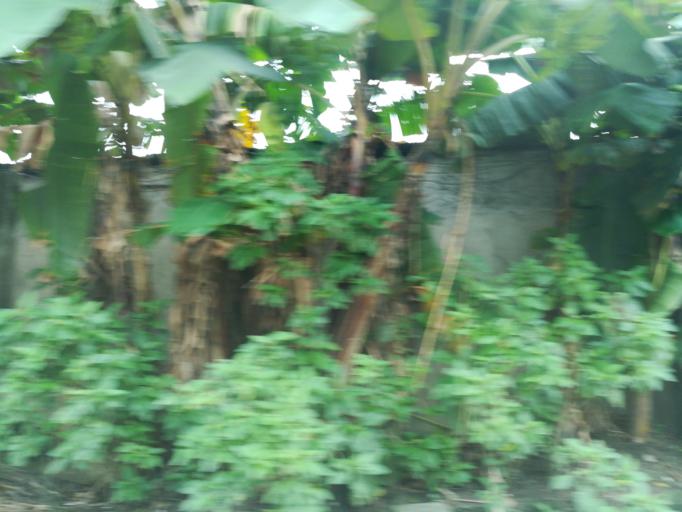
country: NG
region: Rivers
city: Port Harcourt
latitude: 4.7605
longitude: 7.0148
